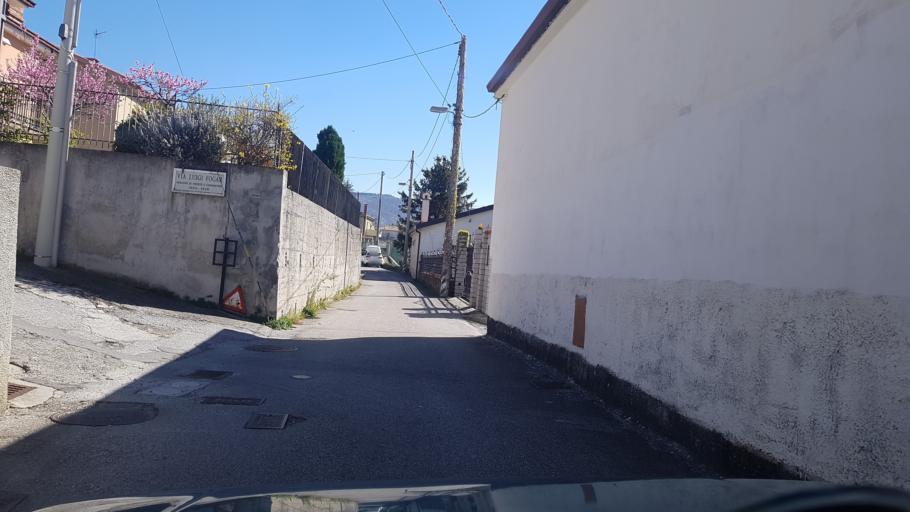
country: IT
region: Friuli Venezia Giulia
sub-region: Provincia di Trieste
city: Domio
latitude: 45.6259
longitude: 13.8162
